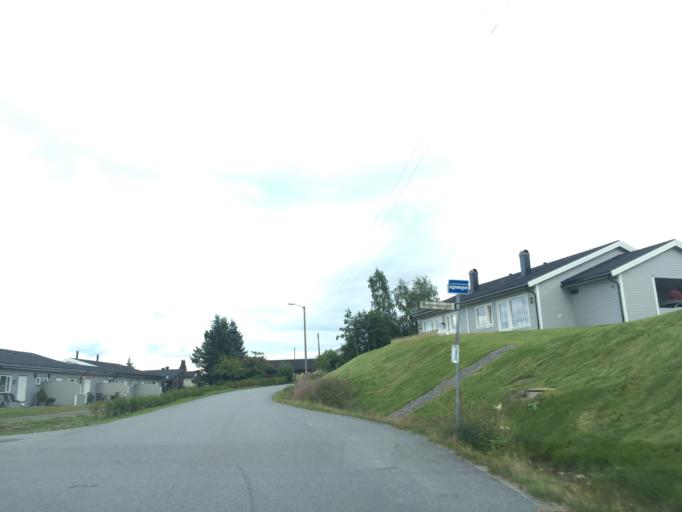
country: NO
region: Hedmark
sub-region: Kongsvinger
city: Kongsvinger
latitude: 60.1832
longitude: 11.9845
